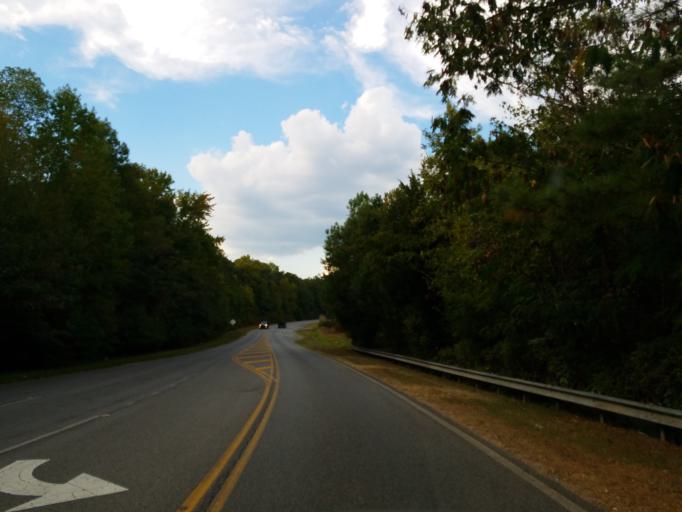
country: US
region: Georgia
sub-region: Monroe County
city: Forsyth
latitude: 33.0418
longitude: -83.9403
